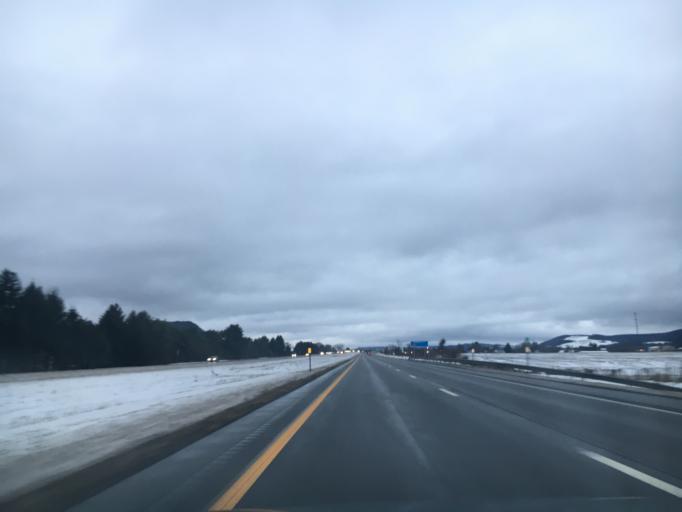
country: US
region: New York
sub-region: Cortland County
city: Homer
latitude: 42.7244
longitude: -76.1446
